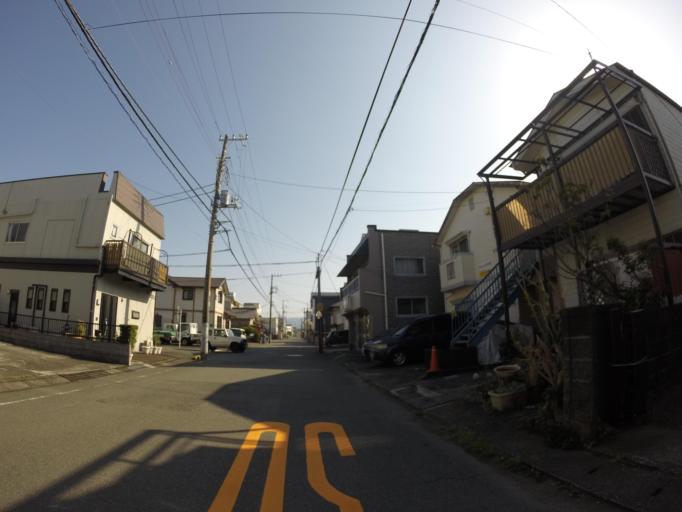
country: JP
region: Shizuoka
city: Numazu
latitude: 35.1024
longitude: 138.8499
